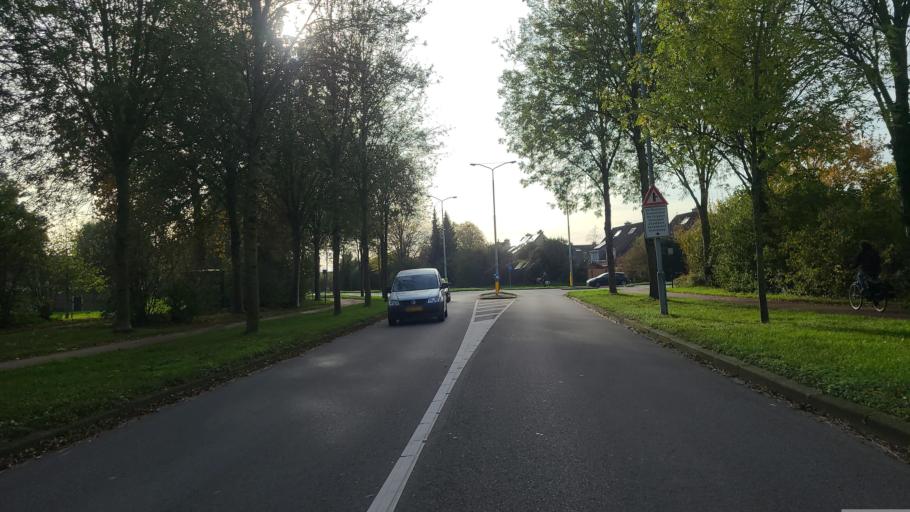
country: NL
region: Gelderland
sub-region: Gemeente Wijchen
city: Wijchen
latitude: 51.8026
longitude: 5.7195
